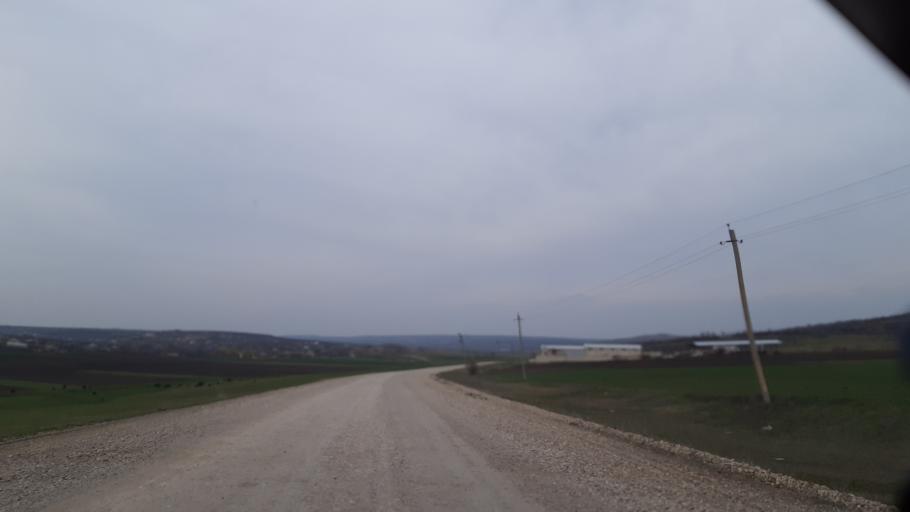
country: MD
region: Soldanesti
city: Soldanesti
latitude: 47.6247
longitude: 28.6581
